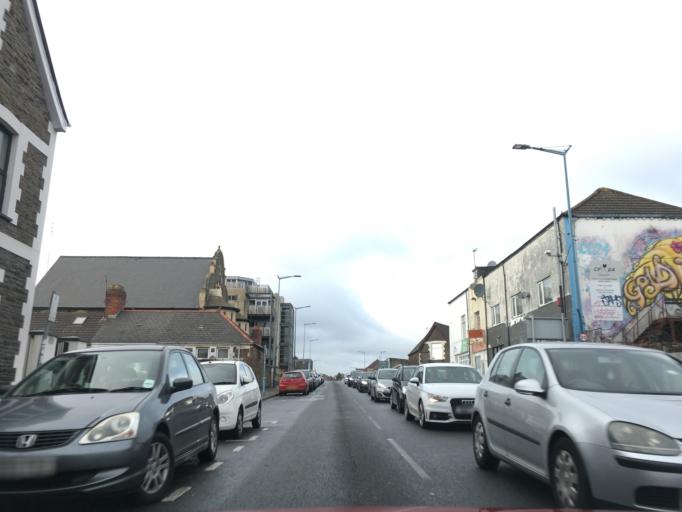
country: GB
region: Wales
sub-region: Cardiff
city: Cardiff
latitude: 51.4930
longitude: -3.1728
